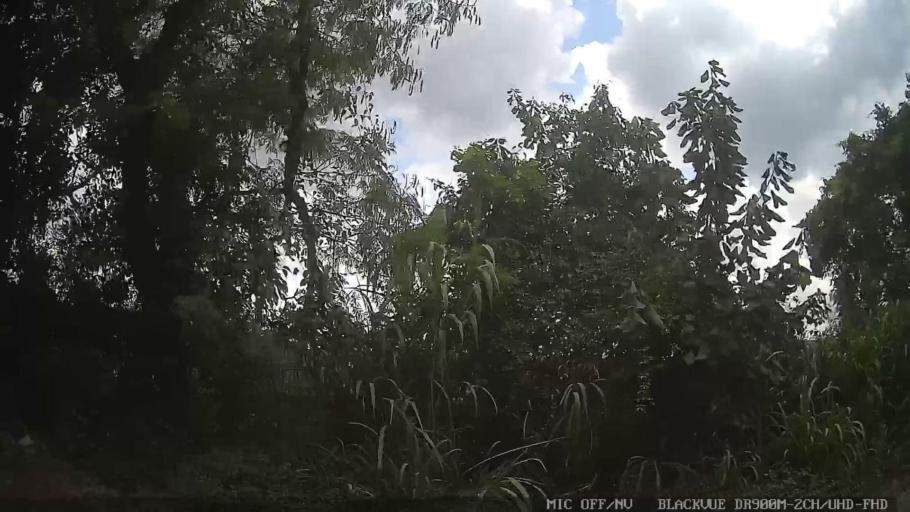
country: BR
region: Sao Paulo
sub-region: Ferraz De Vasconcelos
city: Ferraz de Vasconcelos
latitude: -23.6228
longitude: -46.3871
